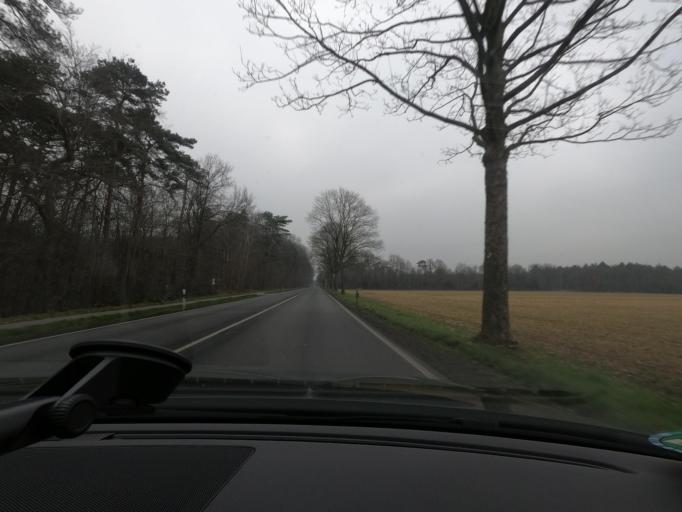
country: DE
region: North Rhine-Westphalia
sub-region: Regierungsbezirk Dusseldorf
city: Nettetal
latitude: 51.3671
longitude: 6.2454
